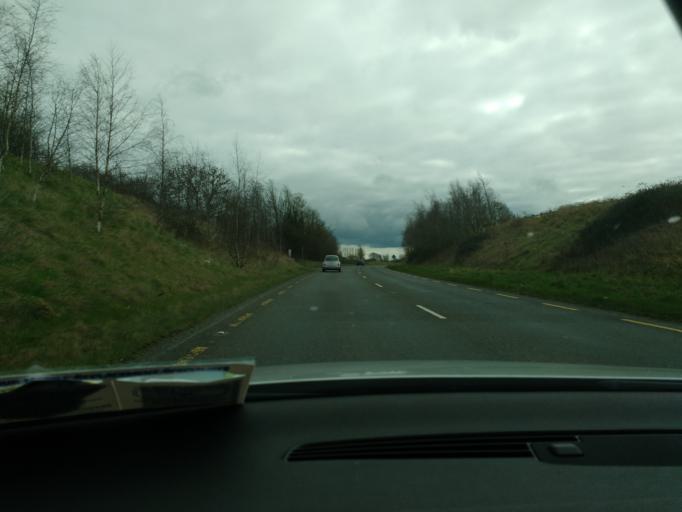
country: IE
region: Leinster
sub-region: Kilkenny
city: Ballyragget
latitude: 52.7165
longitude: -7.3337
